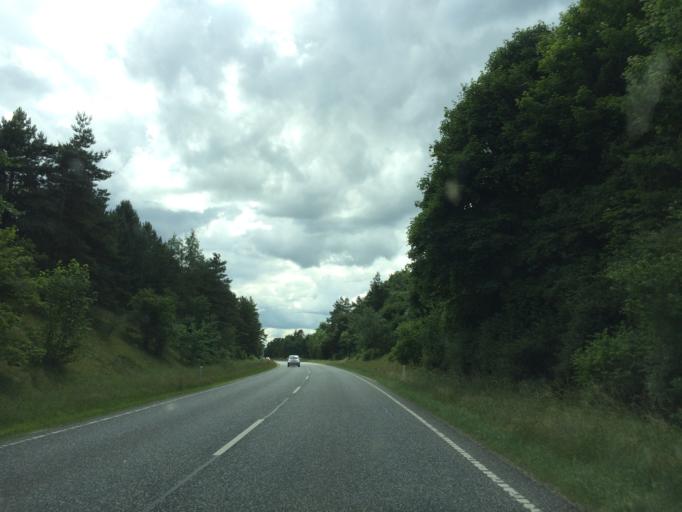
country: DK
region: Central Jutland
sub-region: Viborg Kommune
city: Viborg
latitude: 56.5362
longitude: 9.4636
